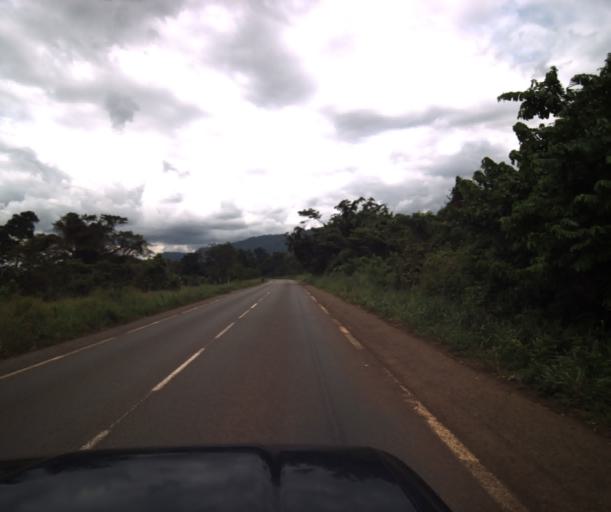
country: CM
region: Centre
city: Eseka
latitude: 3.8806
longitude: 10.8108
